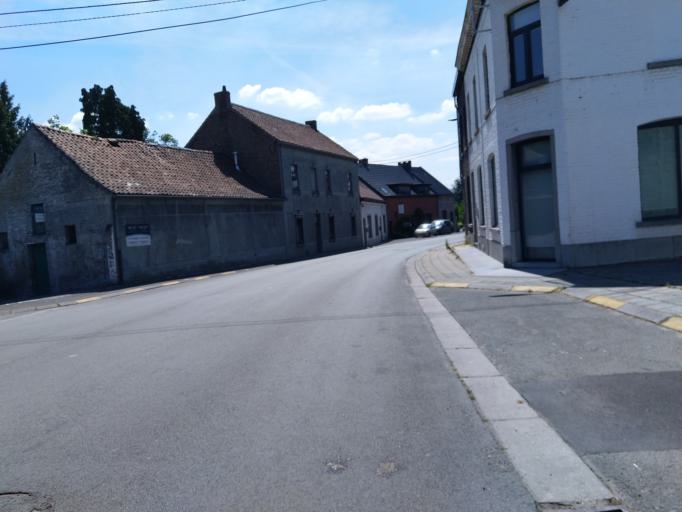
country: BE
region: Wallonia
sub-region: Province du Hainaut
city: Saint-Ghislain
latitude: 50.4830
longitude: 3.8335
